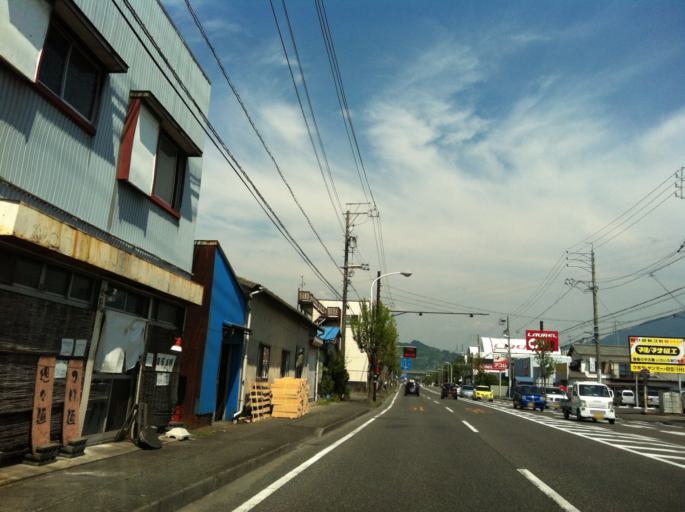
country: JP
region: Shizuoka
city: Shizuoka-shi
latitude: 35.0040
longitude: 138.4053
